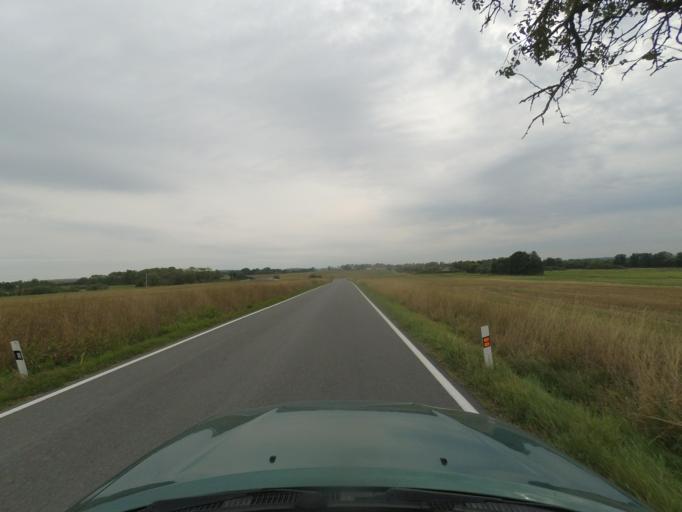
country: CZ
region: Plzensky
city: Meclov
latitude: 49.5374
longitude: 12.8781
